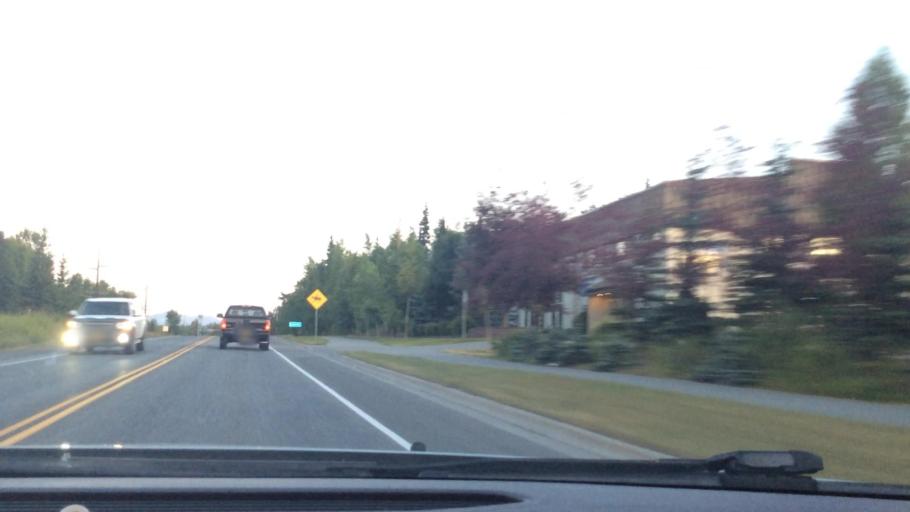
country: US
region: Alaska
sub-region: Anchorage Municipality
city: Anchorage
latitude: 61.1545
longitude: -149.8042
